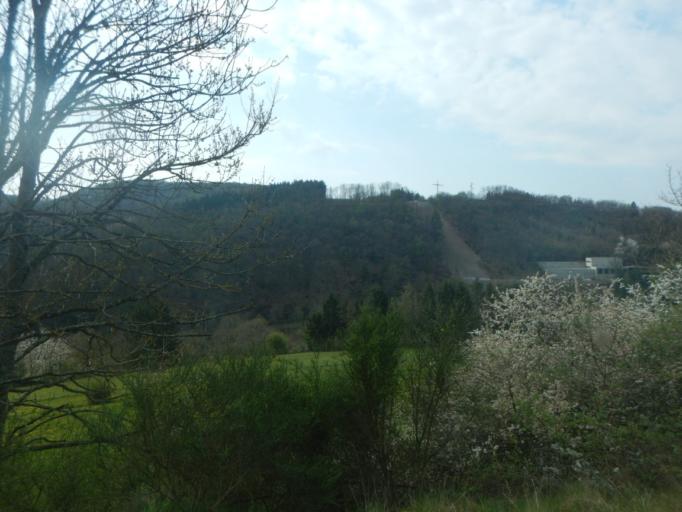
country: LU
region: Diekirch
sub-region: Canton de Wiltz
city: Esch-sur-Sure
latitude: 49.9093
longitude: 5.9299
